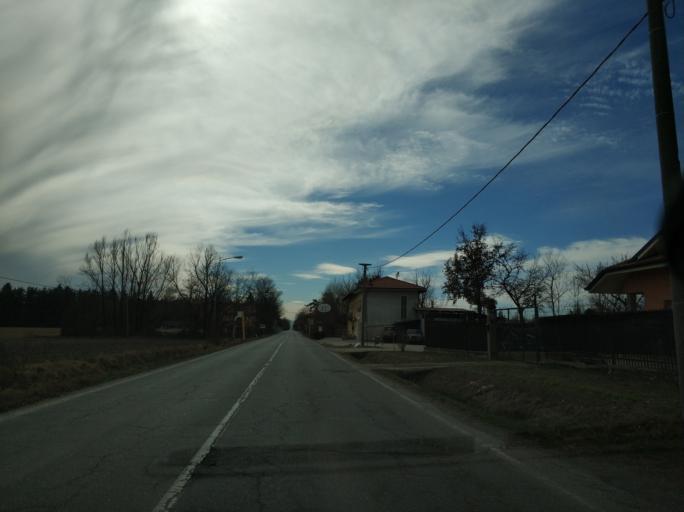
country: IT
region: Piedmont
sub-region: Provincia di Torino
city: Lombardore
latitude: 45.2259
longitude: 7.7316
